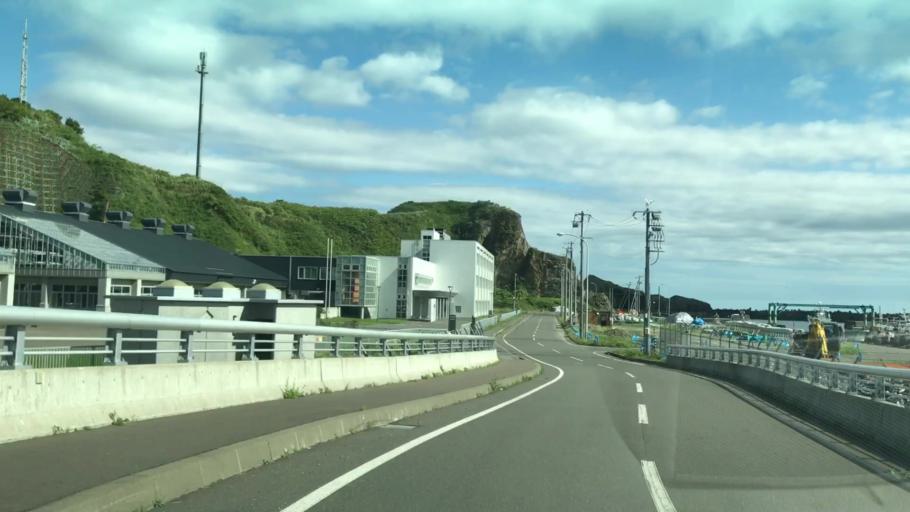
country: JP
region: Hokkaido
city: Muroran
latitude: 42.3097
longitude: 140.9661
